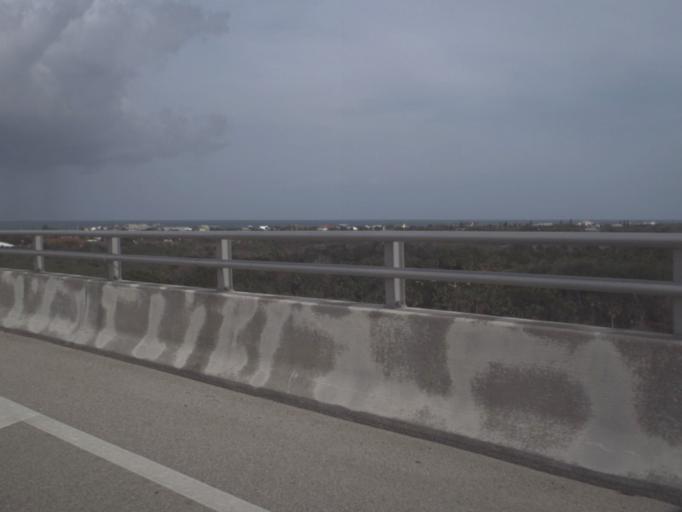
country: US
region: Florida
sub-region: Flagler County
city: Flagler Beach
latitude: 29.4775
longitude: -81.1367
